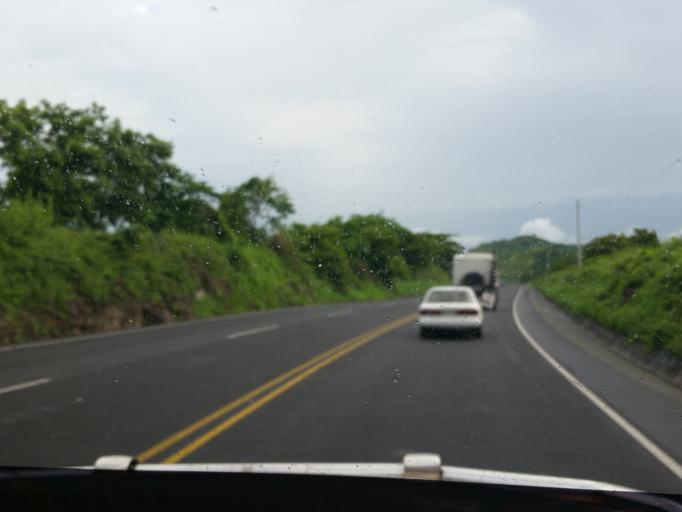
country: NI
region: Matagalpa
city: Ciudad Dario
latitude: 12.5185
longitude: -86.0522
